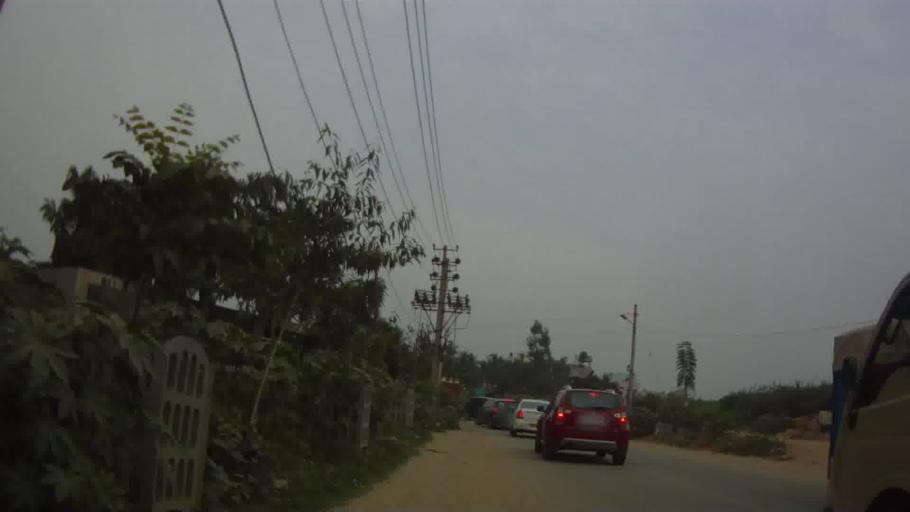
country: IN
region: Karnataka
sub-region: Bangalore Urban
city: Bangalore
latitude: 12.9726
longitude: 77.6998
